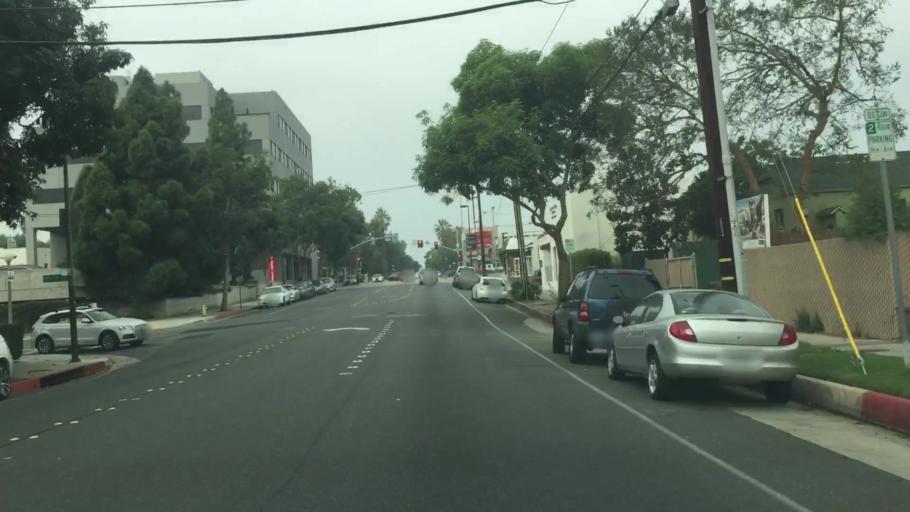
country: US
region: California
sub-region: Los Angeles County
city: Pasadena
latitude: 34.1359
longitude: -118.1306
